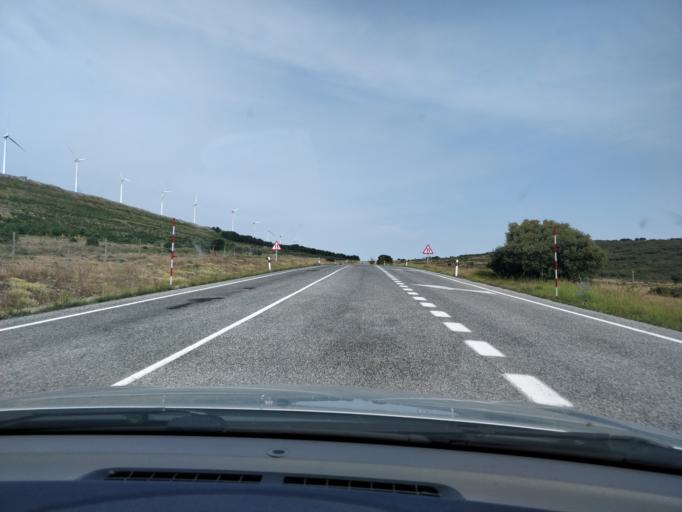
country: ES
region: Castille and Leon
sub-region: Provincia de Burgos
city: Medina de Pomar
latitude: 42.9262
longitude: -3.6358
